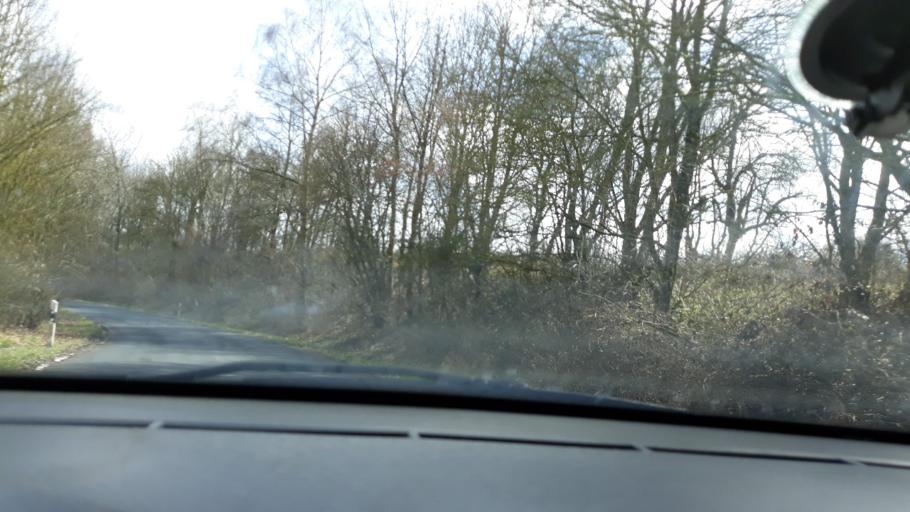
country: DE
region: Saarland
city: Gersheim
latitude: 49.1866
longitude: 7.2219
